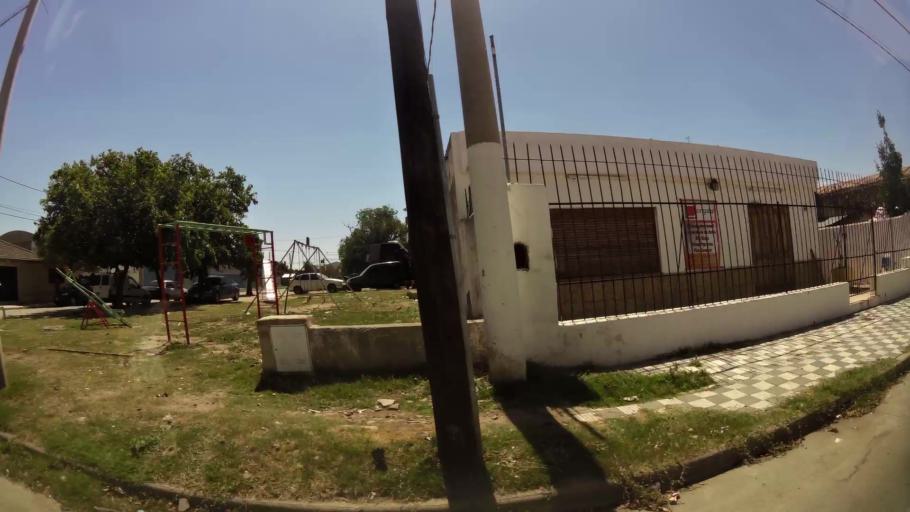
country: AR
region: Cordoba
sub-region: Departamento de Capital
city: Cordoba
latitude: -31.3813
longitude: -64.1494
